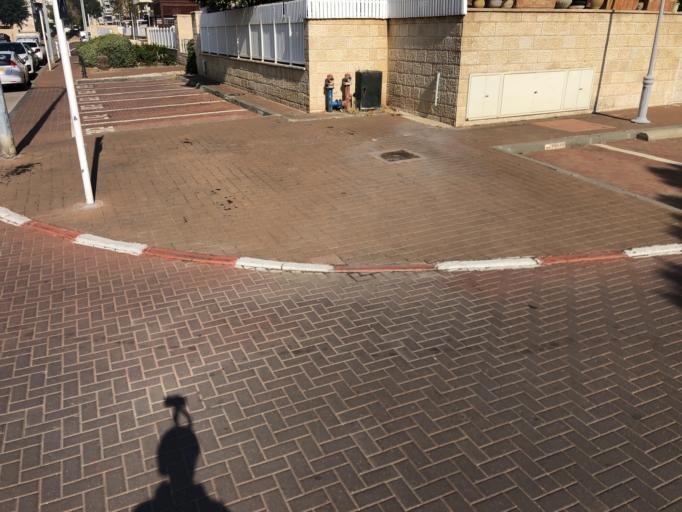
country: IL
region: Northern District
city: `Akko
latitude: 32.9254
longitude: 35.0955
